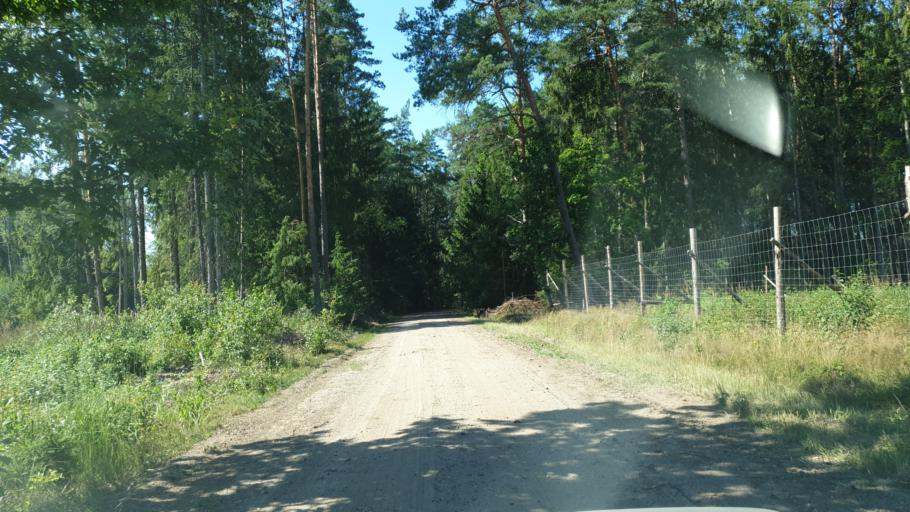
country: LT
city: Sirvintos
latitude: 54.9103
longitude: 24.9353
